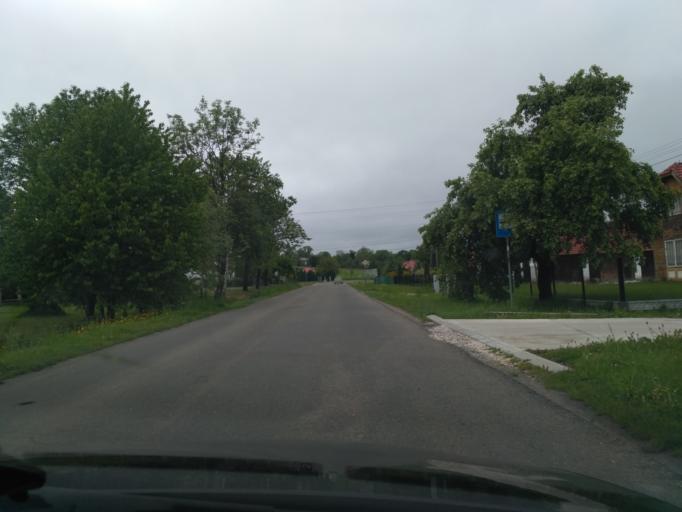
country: PL
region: Subcarpathian Voivodeship
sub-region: Powiat jasielski
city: Brzyska
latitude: 49.8155
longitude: 21.3952
